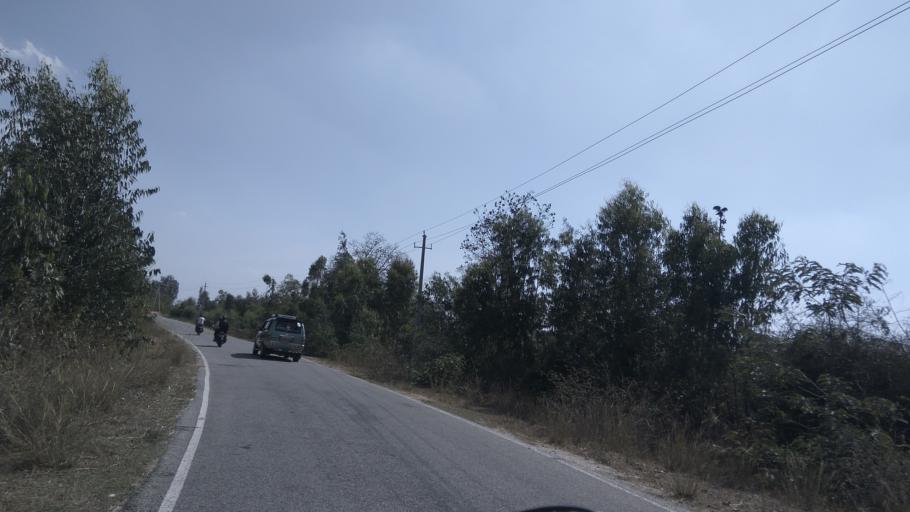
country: IN
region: Karnataka
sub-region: Kolar
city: Mulbagal
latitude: 13.1990
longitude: 78.3549
